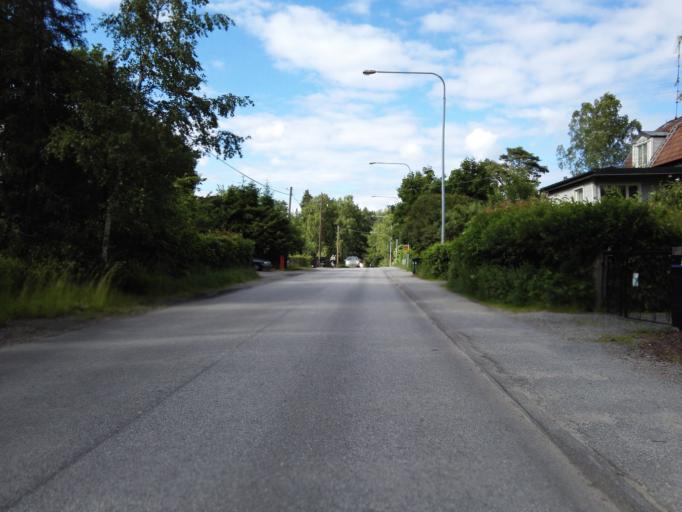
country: SE
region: Stockholm
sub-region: Huddinge Kommun
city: Huddinge
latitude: 59.2554
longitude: 17.9944
